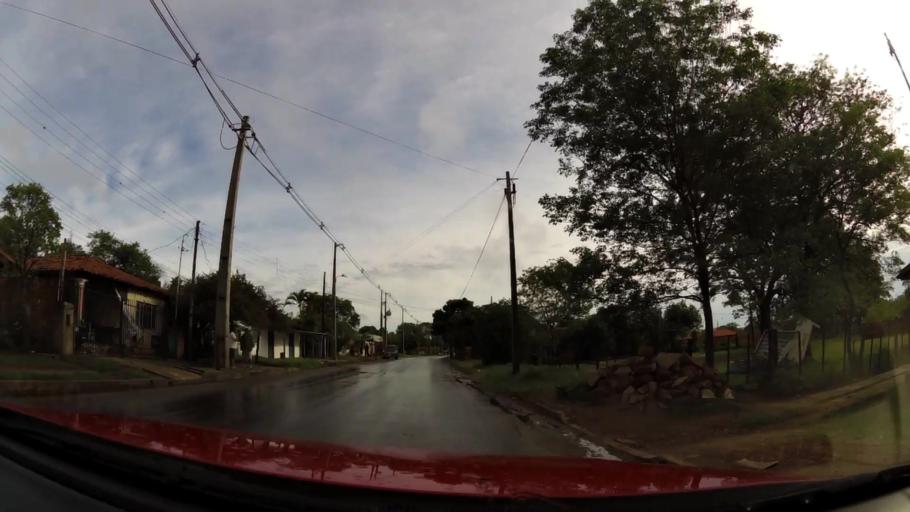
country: PY
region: Central
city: Limpio
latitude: -25.2000
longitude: -57.5033
